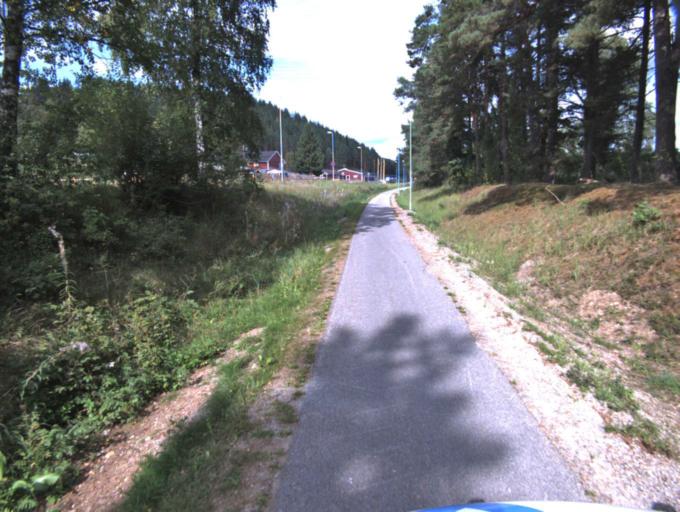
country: SE
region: Vaestra Goetaland
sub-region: Ulricehamns Kommun
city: Ulricehamn
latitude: 57.8184
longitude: 13.4121
